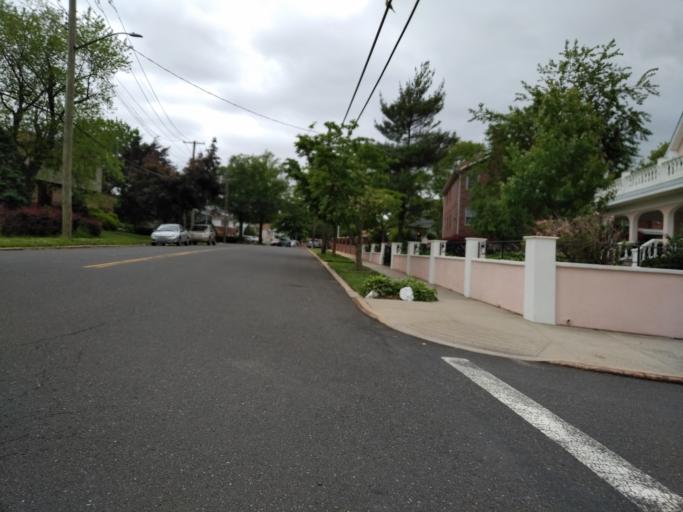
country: US
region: New York
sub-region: Nassau County
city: East Atlantic Beach
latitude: 40.7760
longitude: -73.7791
